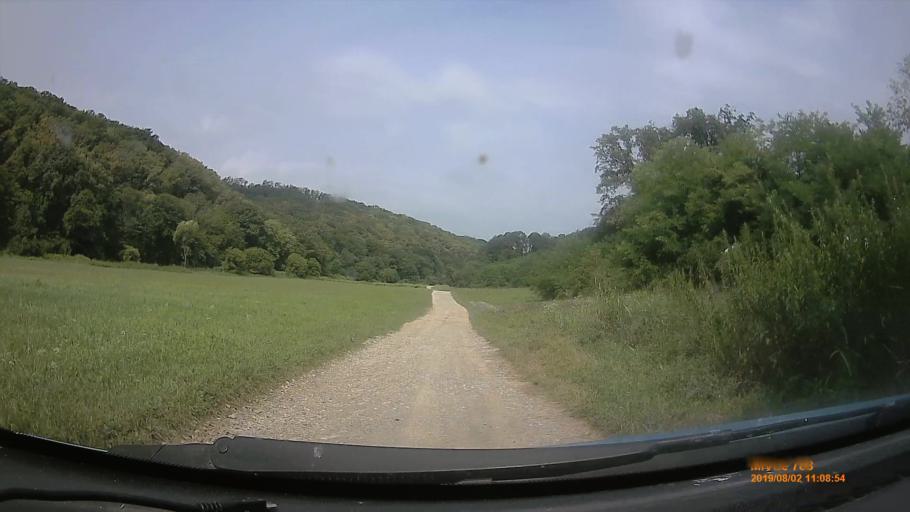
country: HU
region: Baranya
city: Buekkoesd
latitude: 46.1011
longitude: 17.9423
